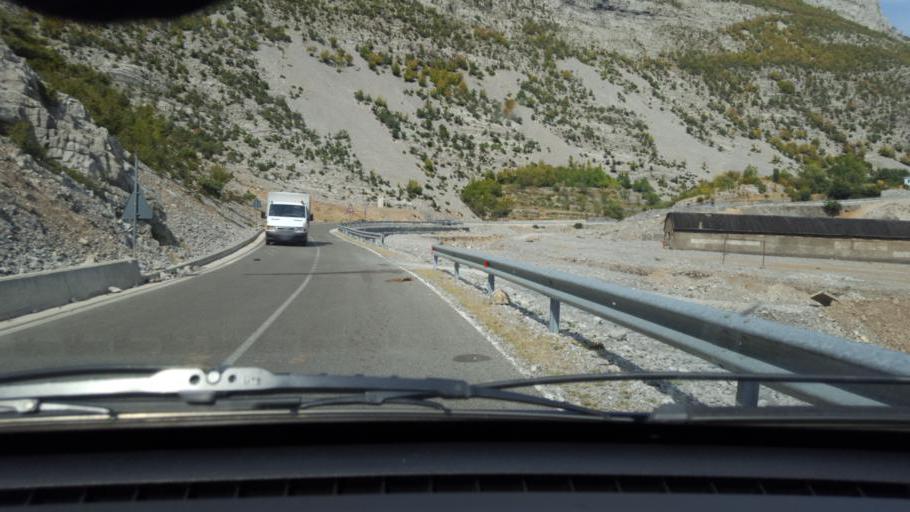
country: AL
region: Shkoder
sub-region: Rrethi i Malesia e Madhe
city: Kastrat
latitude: 42.4970
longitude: 19.5813
